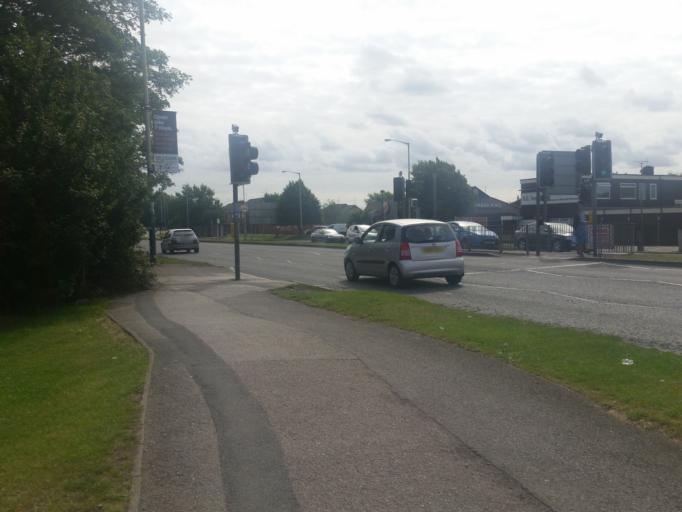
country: GB
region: England
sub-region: Borough of Swindon
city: Swindon
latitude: 51.5629
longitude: -1.7708
